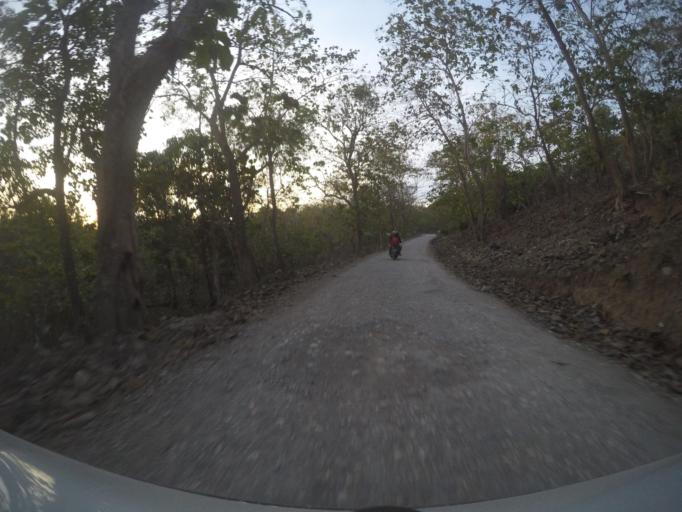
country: TL
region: Viqueque
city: Viqueque
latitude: -8.8961
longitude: 126.3891
